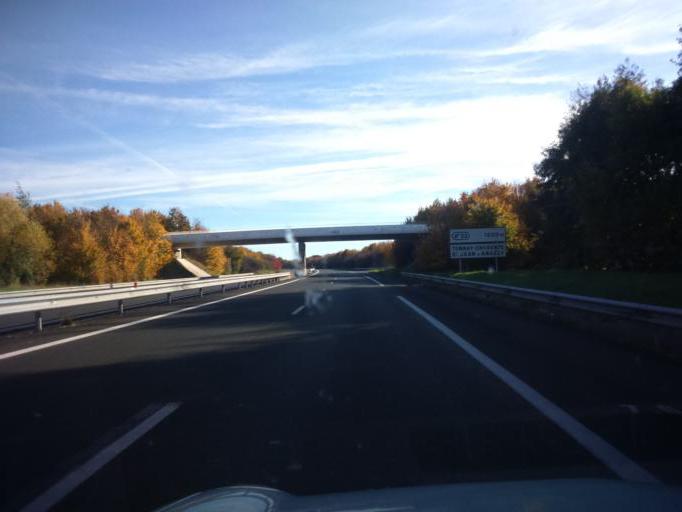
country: FR
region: Poitou-Charentes
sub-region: Departement de la Charente-Maritime
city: Tonnay-Charente
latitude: 45.9545
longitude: -0.9004
